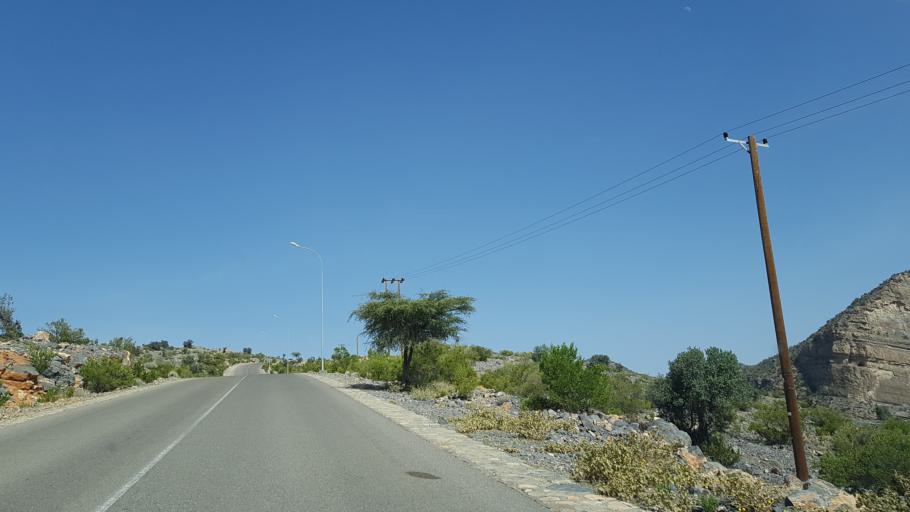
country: OM
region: Al Batinah
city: Bayt al `Awabi
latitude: 23.1369
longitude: 57.5527
